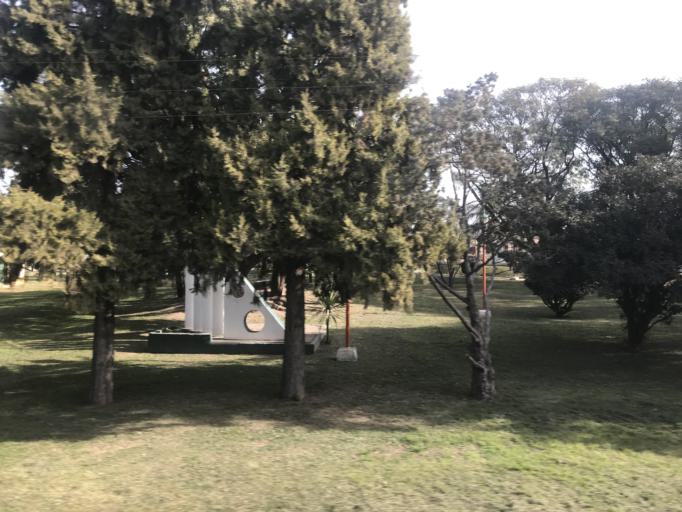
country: AR
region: Cordoba
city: Laguna Larga
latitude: -31.7752
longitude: -63.8046
